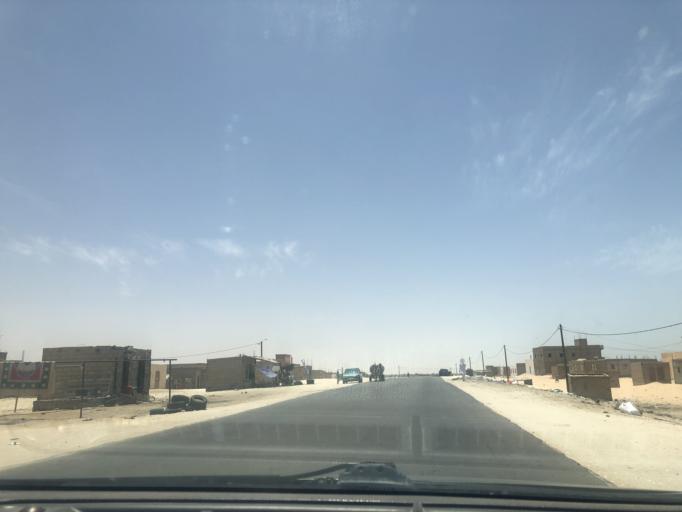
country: MR
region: Nouakchott
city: Nouakchott
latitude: 18.0065
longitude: -15.9597
